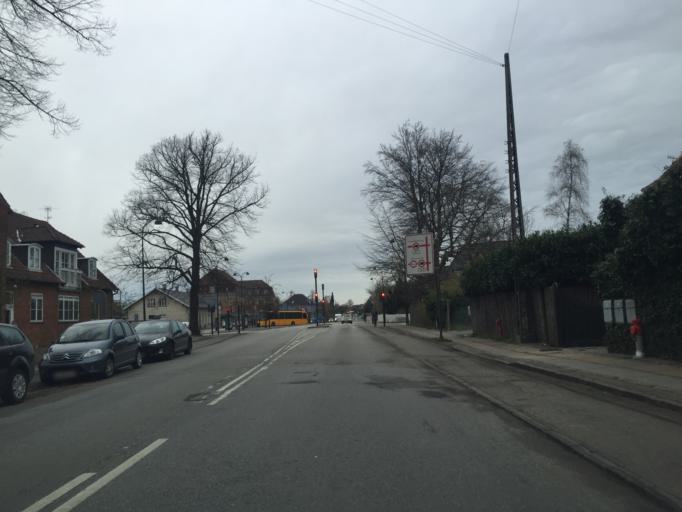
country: DK
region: Capital Region
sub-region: Gentofte Kommune
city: Charlottenlund
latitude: 55.7298
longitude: 12.5685
